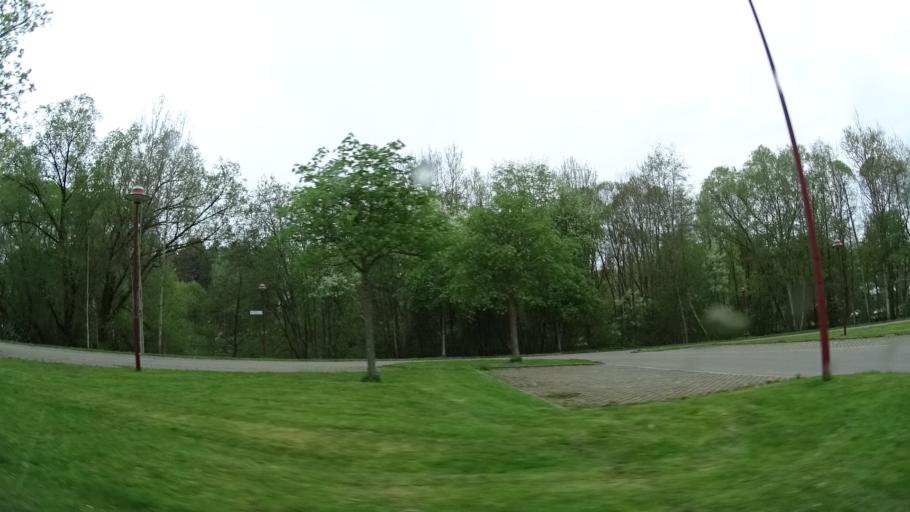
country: DE
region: Baden-Wuerttemberg
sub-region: Freiburg Region
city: Niedereschach
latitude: 48.1282
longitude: 8.5256
